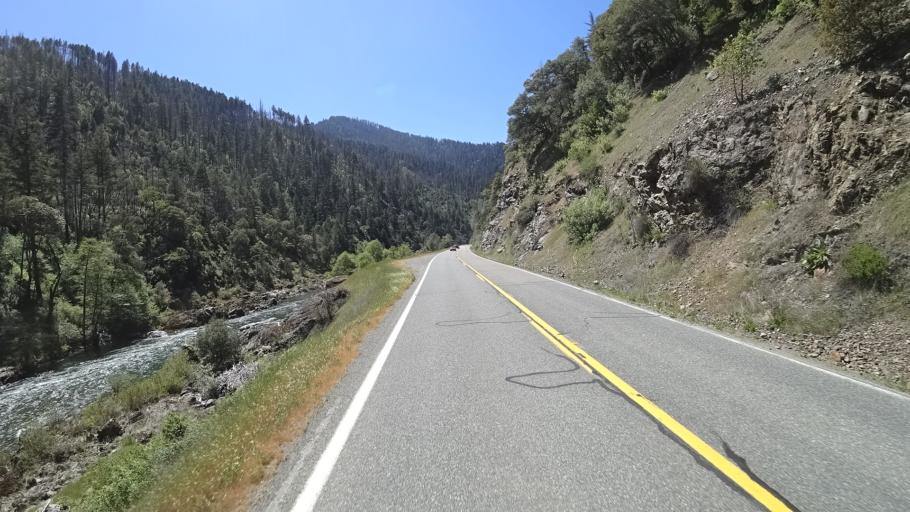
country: US
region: California
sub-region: Trinity County
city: Hayfork
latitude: 40.7672
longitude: -123.2989
